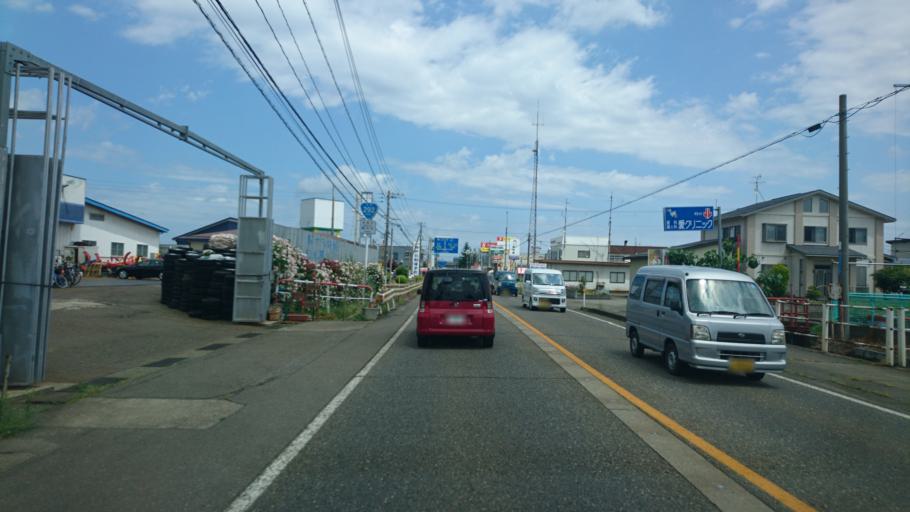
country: JP
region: Niigata
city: Arai
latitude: 37.0564
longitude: 138.2603
